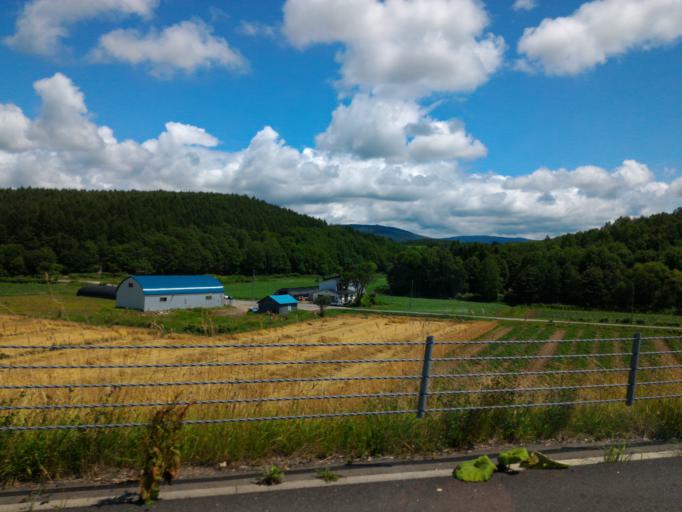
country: JP
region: Hokkaido
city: Nayoro
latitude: 44.4121
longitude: 142.4046
